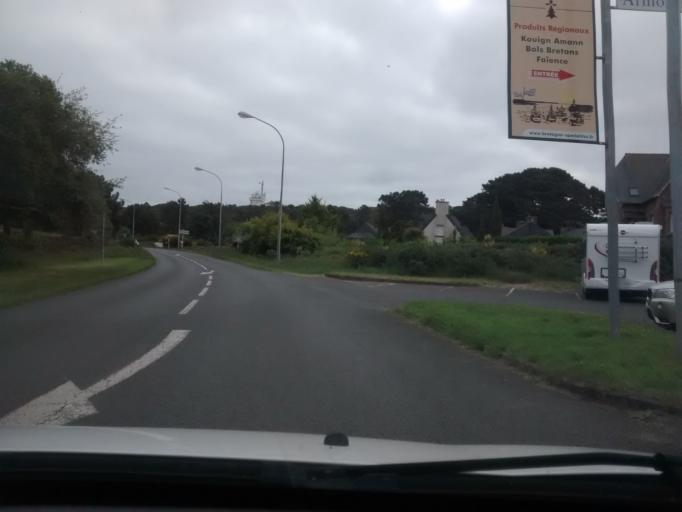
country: FR
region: Brittany
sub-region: Departement des Cotes-d'Armor
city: Tregastel
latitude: 48.8242
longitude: -3.4779
